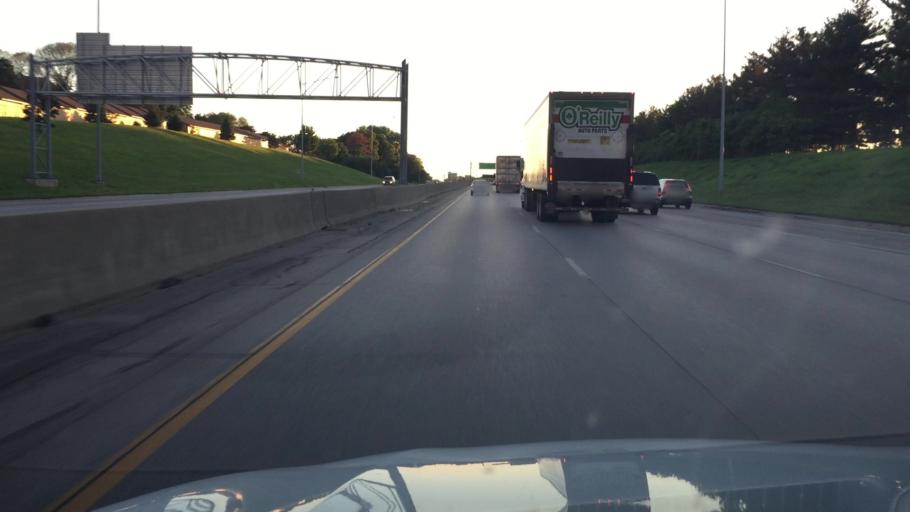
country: US
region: Iowa
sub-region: Polk County
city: Clive
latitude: 41.5934
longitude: -93.7193
